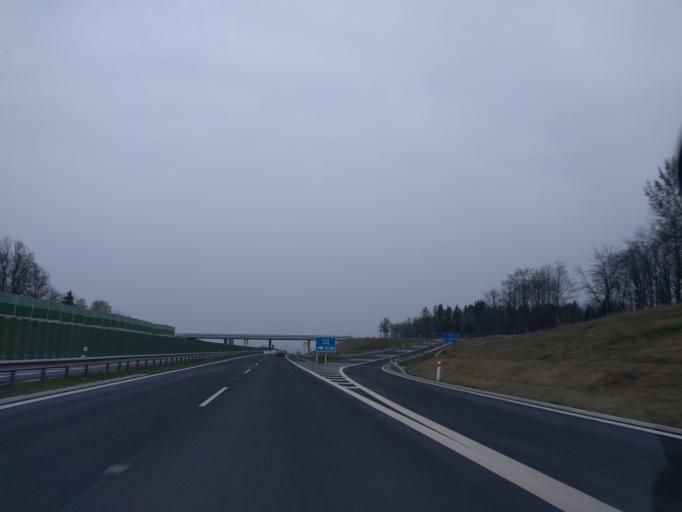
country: CZ
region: Ustecky
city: Lubenec
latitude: 50.1342
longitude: 13.2326
